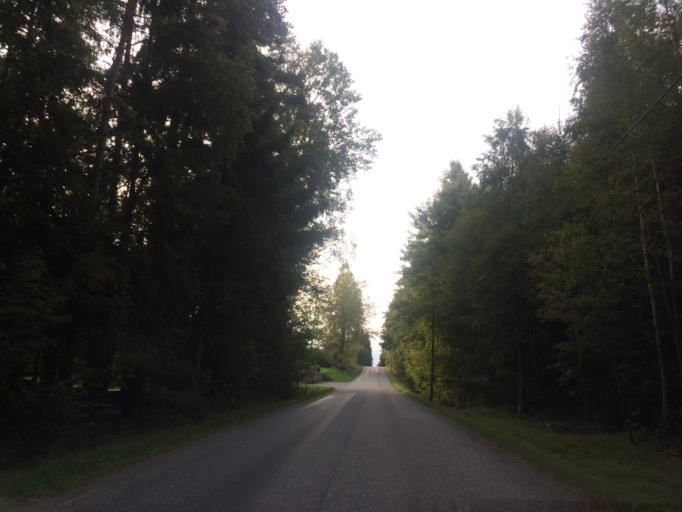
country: SE
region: Vaestra Goetaland
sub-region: Alingsas Kommun
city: Alingsas
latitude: 58.0142
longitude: 12.5460
